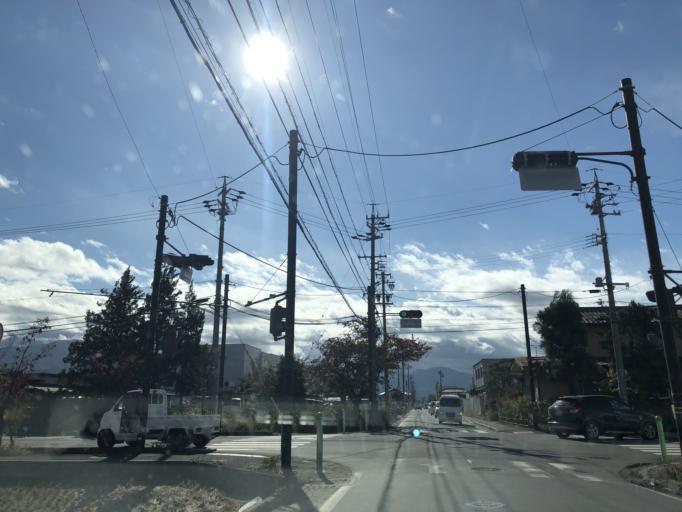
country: JP
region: Nagano
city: Suzaka
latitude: 36.6710
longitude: 138.2579
